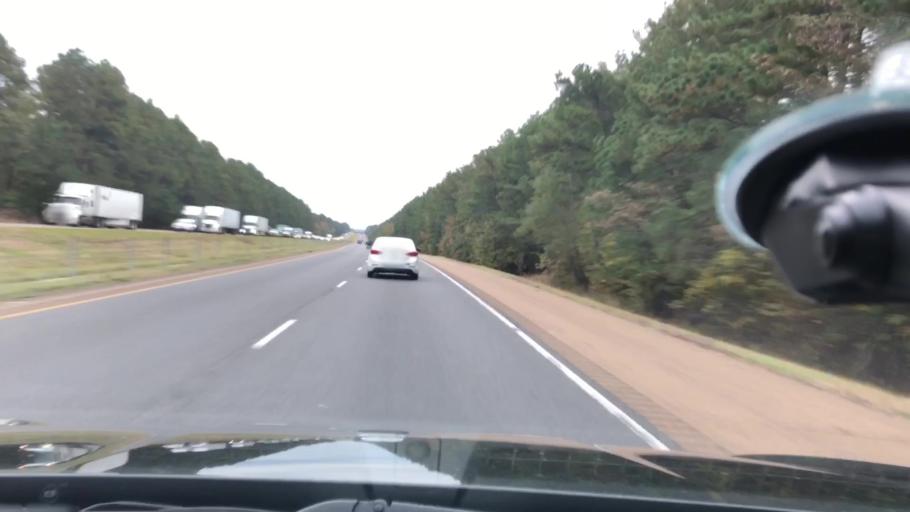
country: US
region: Arkansas
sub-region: Clark County
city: Gurdon
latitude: 33.9590
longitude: -93.2211
